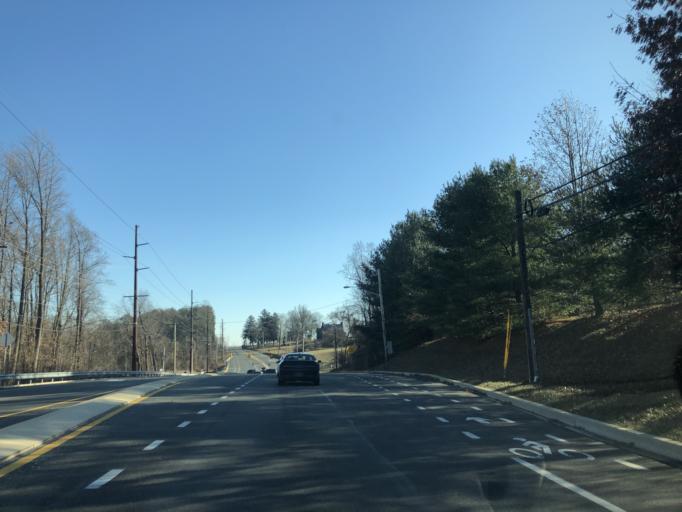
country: US
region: Delaware
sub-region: New Castle County
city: Pike Creek Valley
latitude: 39.7543
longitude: -75.6538
